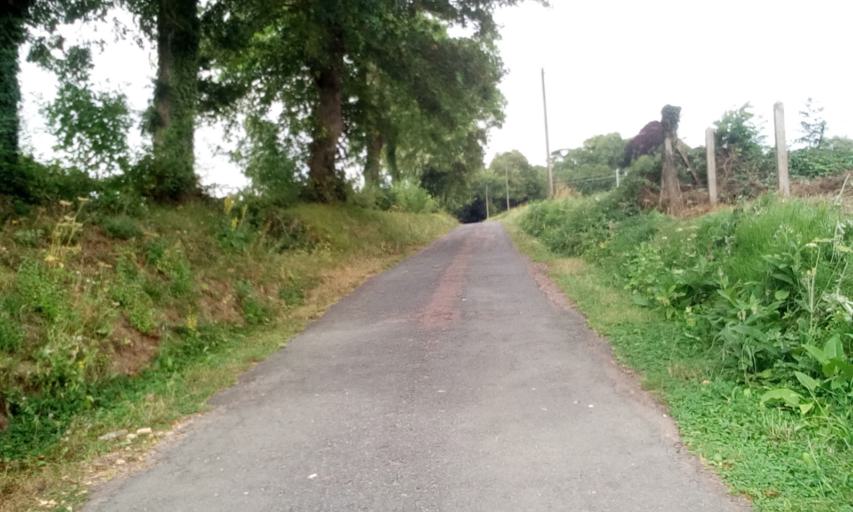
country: FR
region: Lower Normandy
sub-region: Departement du Calvados
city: Tilly-sur-Seulles
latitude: 49.2147
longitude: -0.6236
